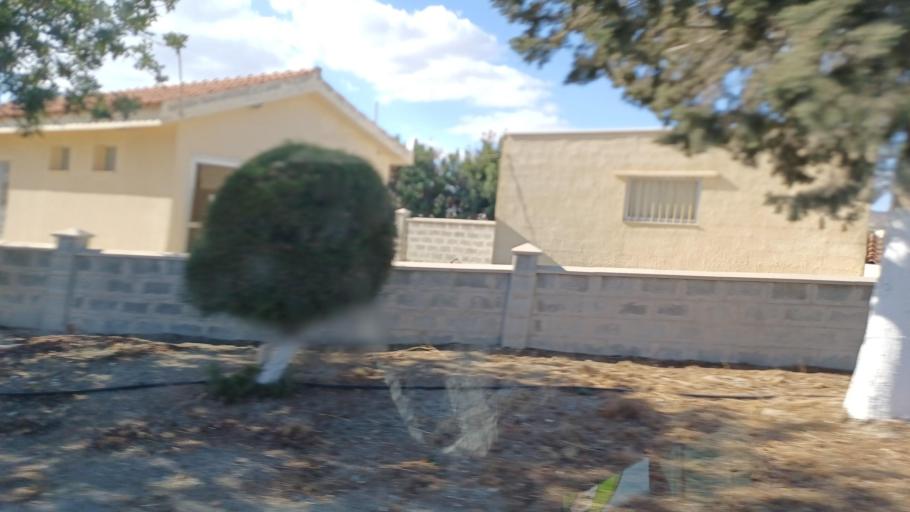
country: CY
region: Limassol
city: Pyrgos
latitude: 34.7306
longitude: 33.2048
